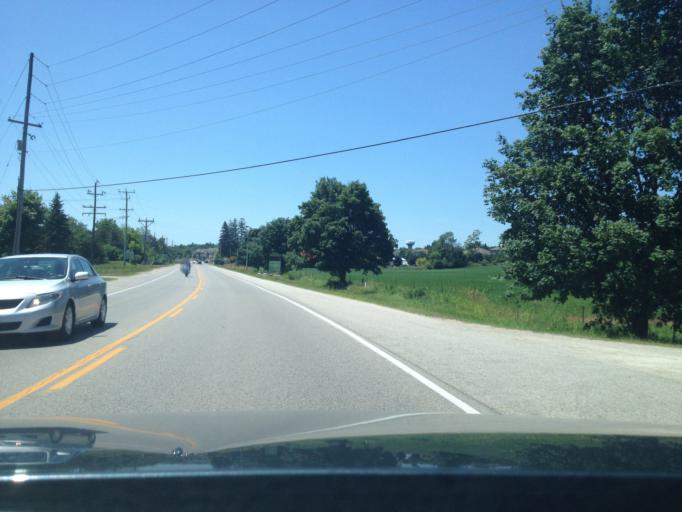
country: CA
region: Ontario
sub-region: Wellington County
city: Guelph
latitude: 43.6926
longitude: -80.4096
